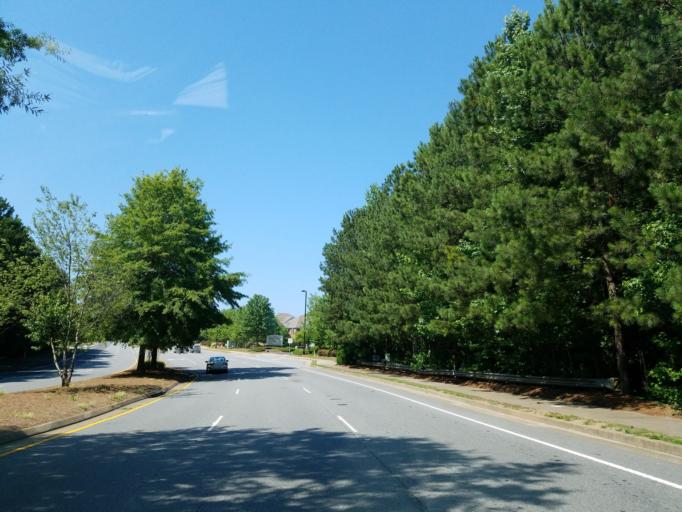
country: US
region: Georgia
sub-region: Fulton County
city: Alpharetta
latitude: 34.0540
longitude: -84.2782
